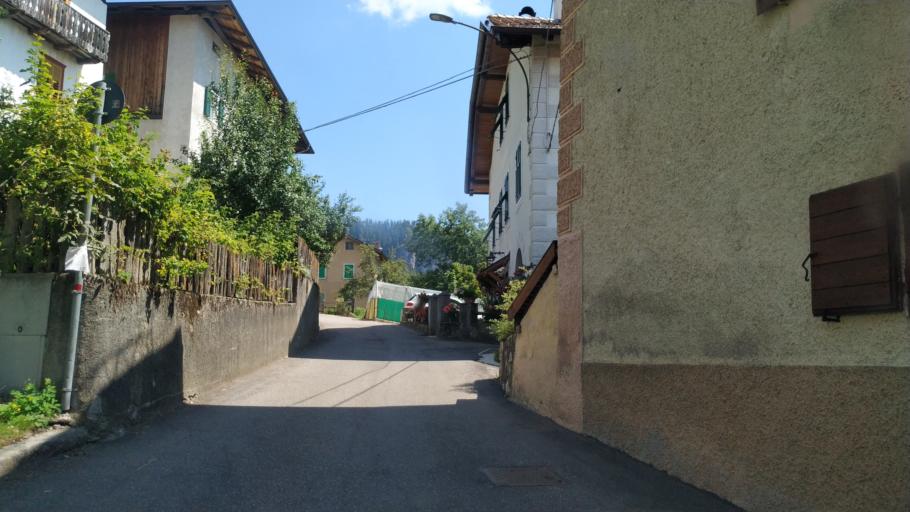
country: IT
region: Trentino-Alto Adige
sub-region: Bolzano
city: San Felice
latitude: 46.4784
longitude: 11.1374
